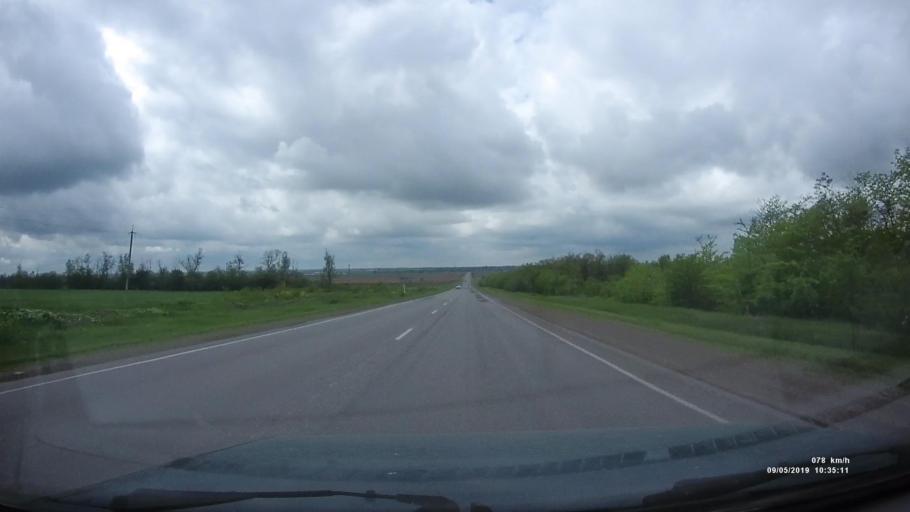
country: RU
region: Rostov
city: Peshkovo
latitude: 47.0464
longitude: 39.4143
